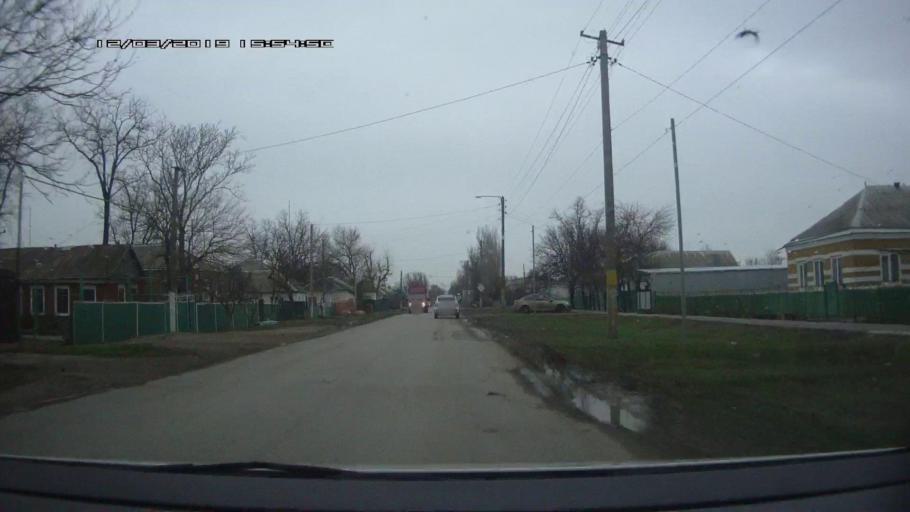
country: RU
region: Rostov
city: Novobataysk
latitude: 46.8931
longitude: 39.7785
